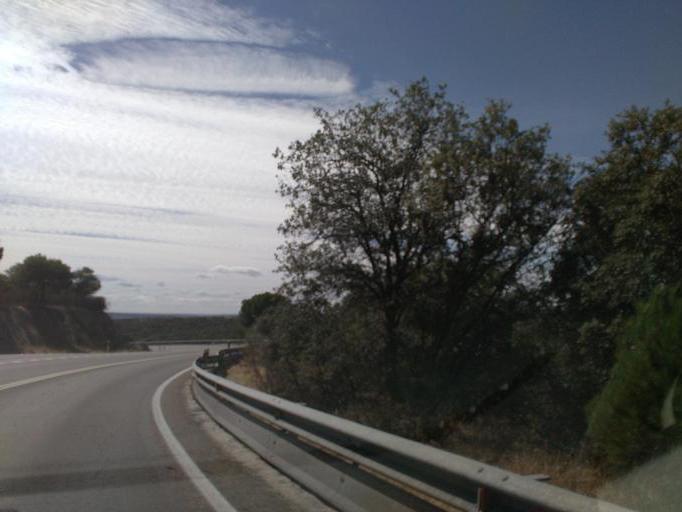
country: ES
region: Madrid
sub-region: Provincia de Madrid
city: Torrelodones
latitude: 40.5397
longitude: -3.9556
